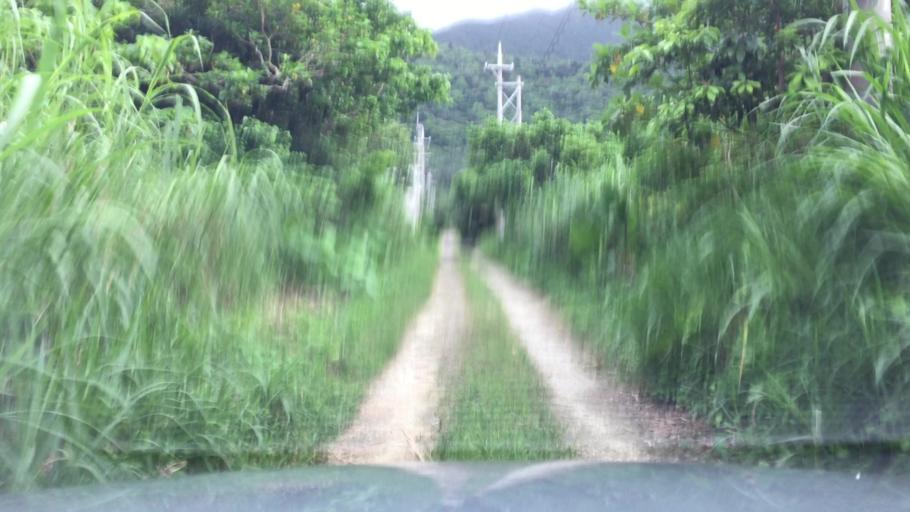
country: JP
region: Okinawa
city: Ishigaki
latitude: 24.4549
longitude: 124.1961
